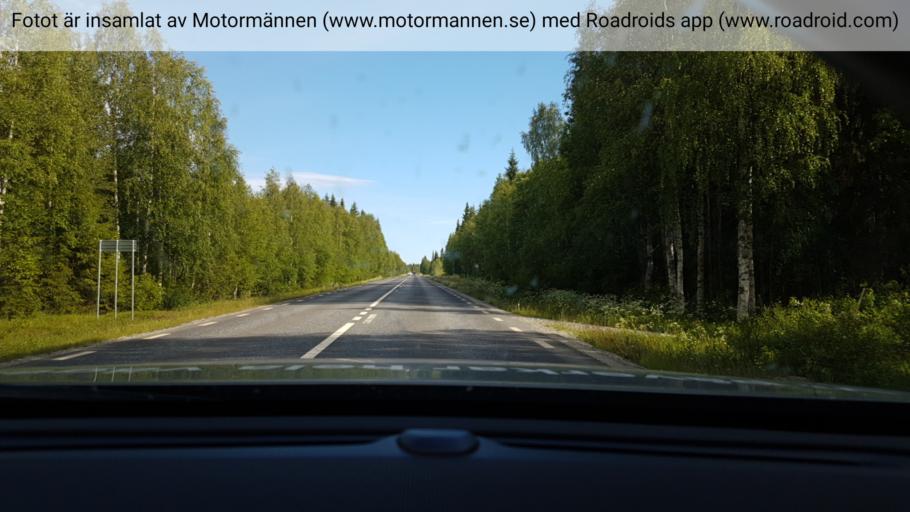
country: SE
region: Vaesterbotten
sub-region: Lycksele Kommun
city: Soderfors
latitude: 64.8245
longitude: 18.0569
